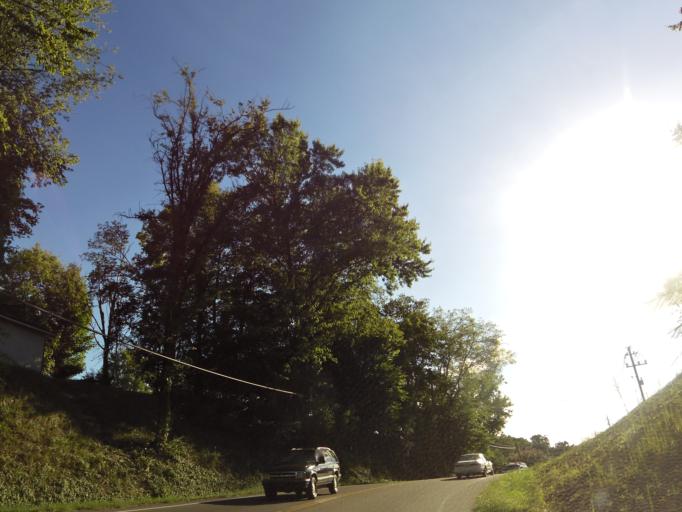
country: US
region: Tennessee
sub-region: Cocke County
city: Newport
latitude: 35.9755
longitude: -83.1754
